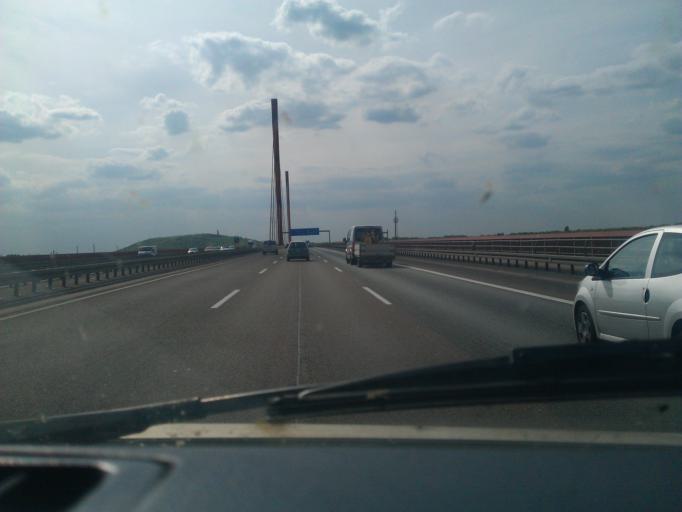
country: DE
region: North Rhine-Westphalia
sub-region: Regierungsbezirk Dusseldorf
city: Moers
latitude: 51.4809
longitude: 6.6879
